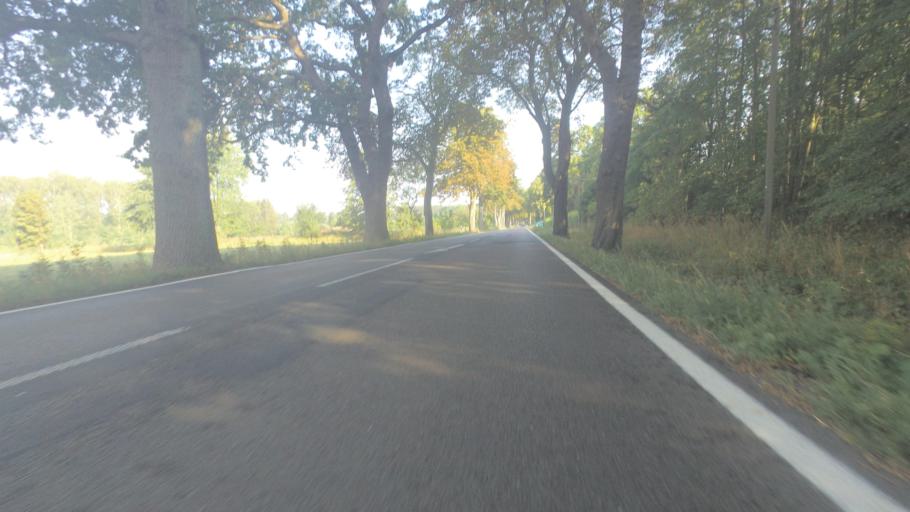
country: DE
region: Mecklenburg-Vorpommern
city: Grimmen
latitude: 54.0621
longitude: 13.1184
